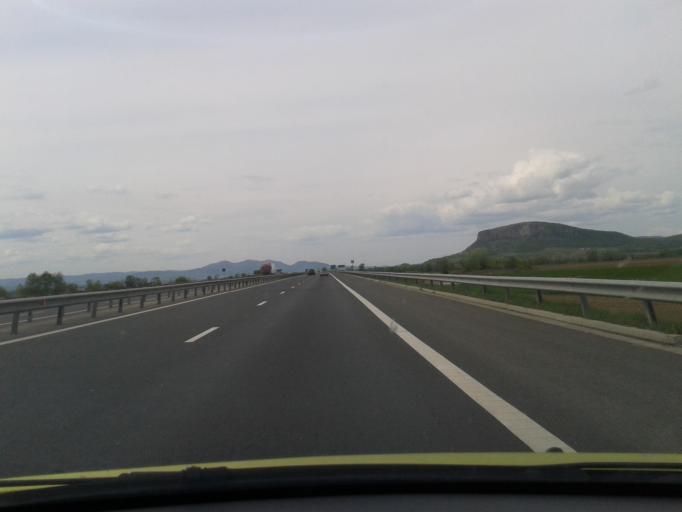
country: RO
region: Hunedoara
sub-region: Comuna Rapoltu Mare
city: Rapoltu Mare
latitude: 45.8416
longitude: 23.0819
